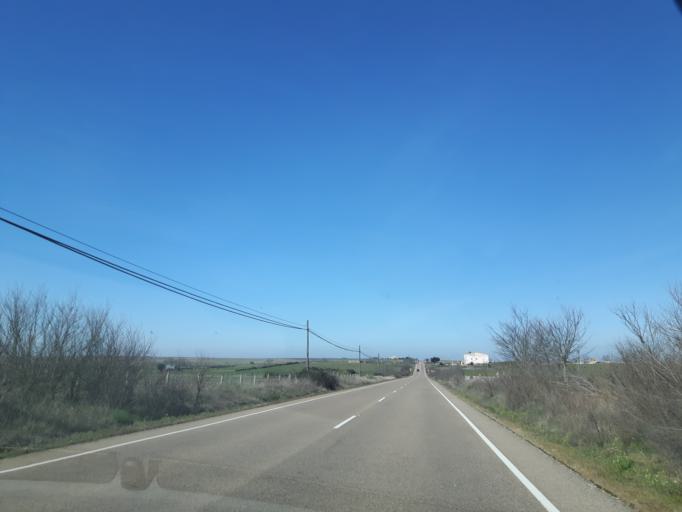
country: ES
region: Castille and Leon
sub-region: Provincia de Salamanca
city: Vitigudino
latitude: 41.0111
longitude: -6.4611
